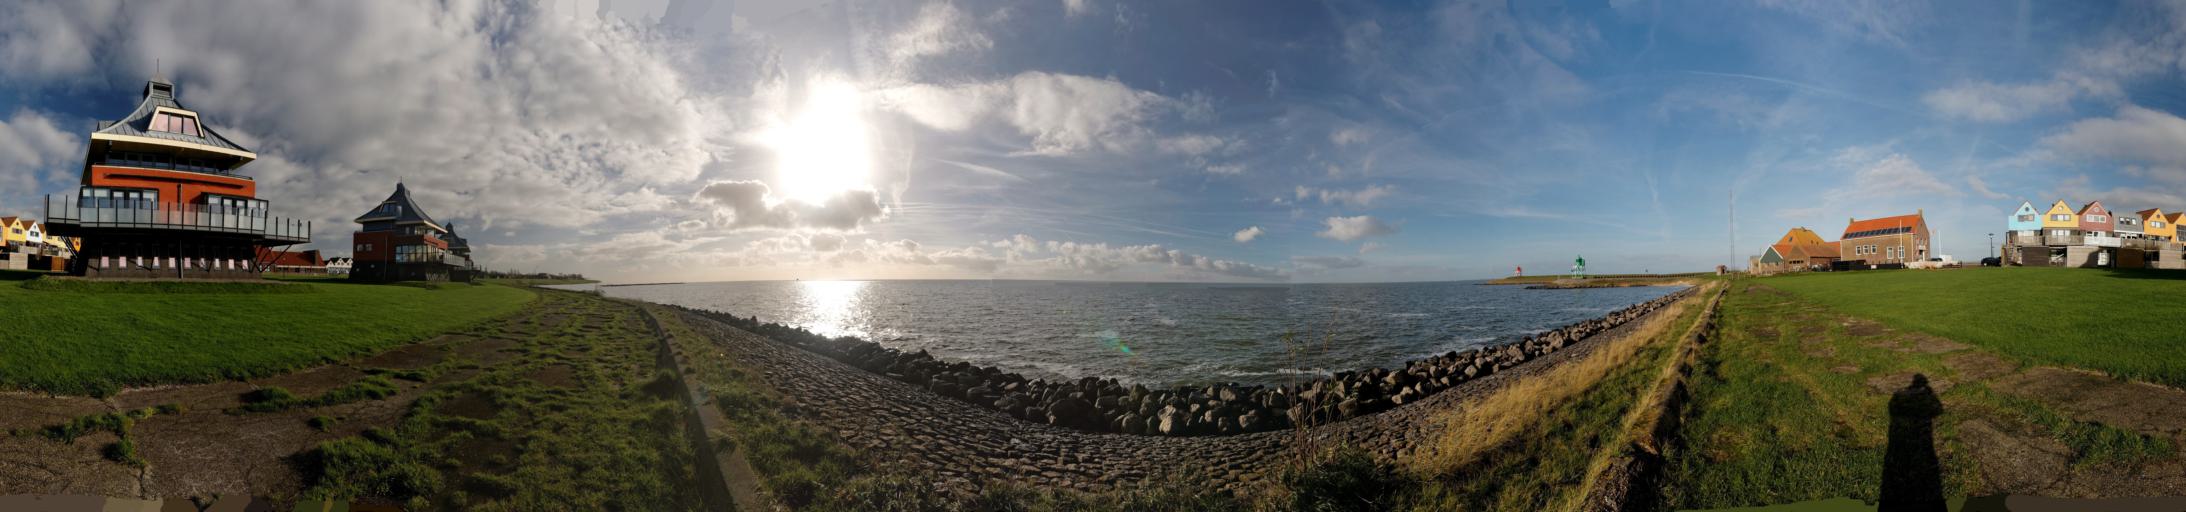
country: NL
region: Friesland
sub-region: Sudwest Fryslan
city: Koudum
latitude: 52.8853
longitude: 5.3550
